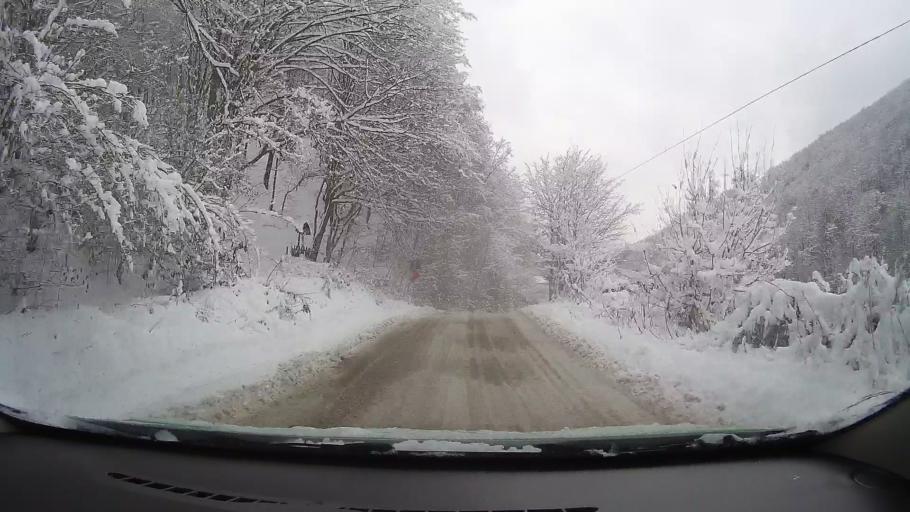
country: RO
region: Alba
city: Pianu de Sus
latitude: 45.8659
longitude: 23.4976
